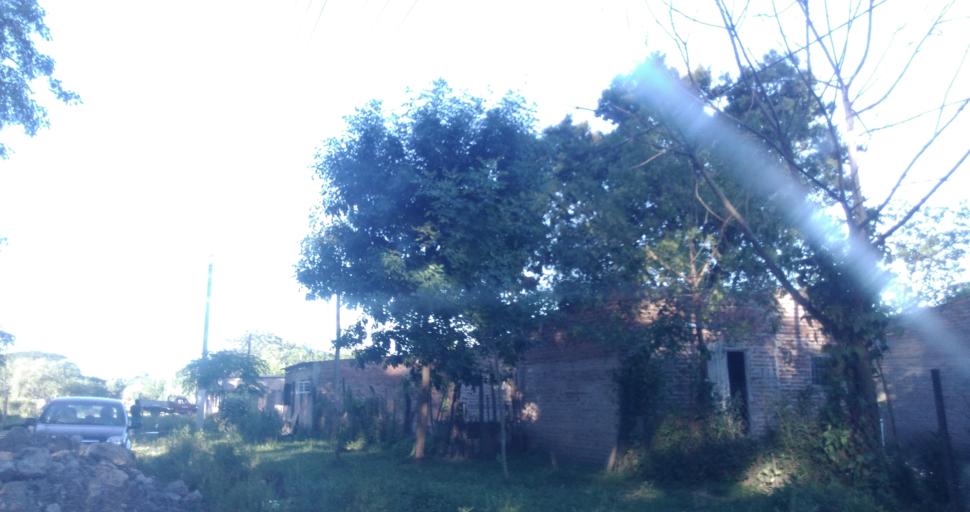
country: AR
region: Chaco
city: Fontana
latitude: -27.4185
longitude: -58.9841
